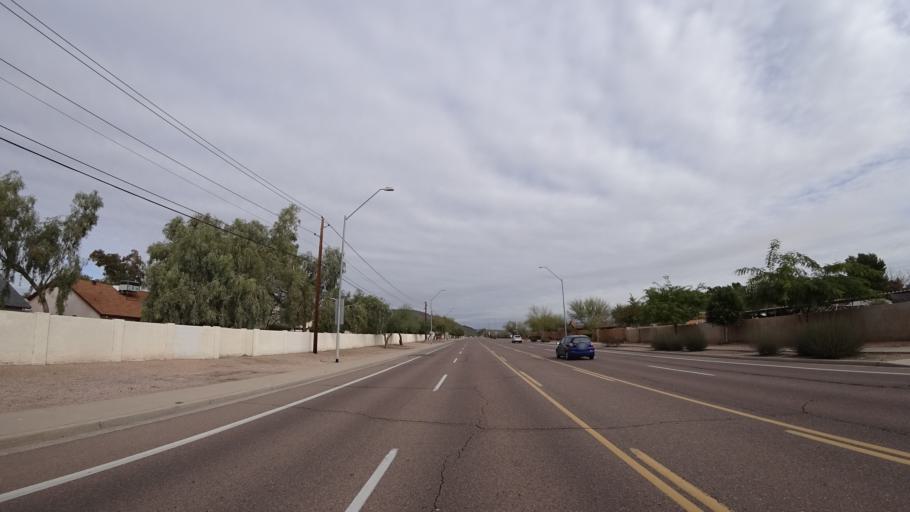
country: US
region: Arizona
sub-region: Maricopa County
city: Peoria
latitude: 33.6606
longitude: -112.1521
